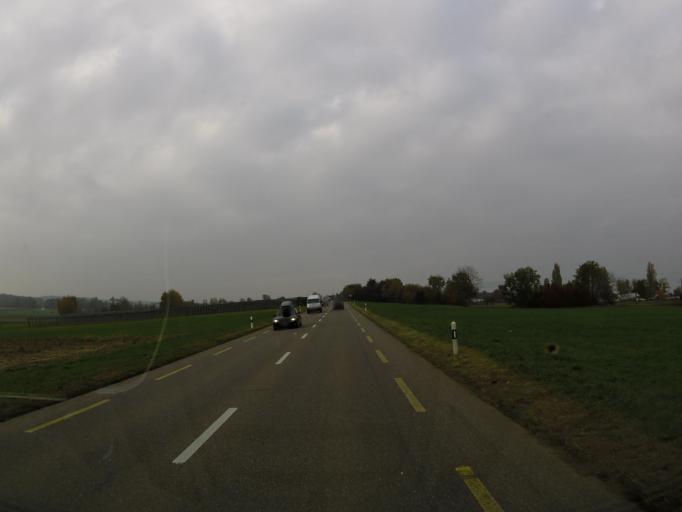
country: CH
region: Thurgau
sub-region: Kreuzlingen District
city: Altnau
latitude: 47.6226
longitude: 9.2588
